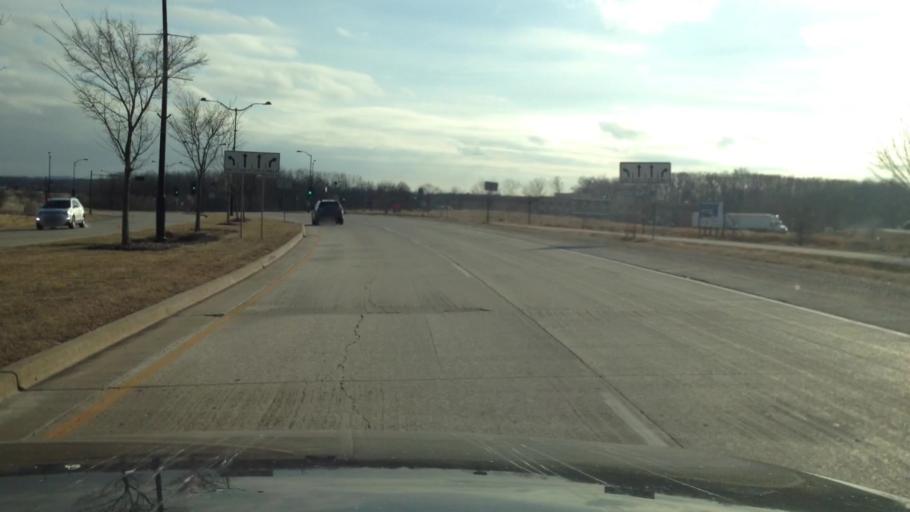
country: US
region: Wisconsin
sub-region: Waukesha County
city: Muskego
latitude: 42.9283
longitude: -88.1143
